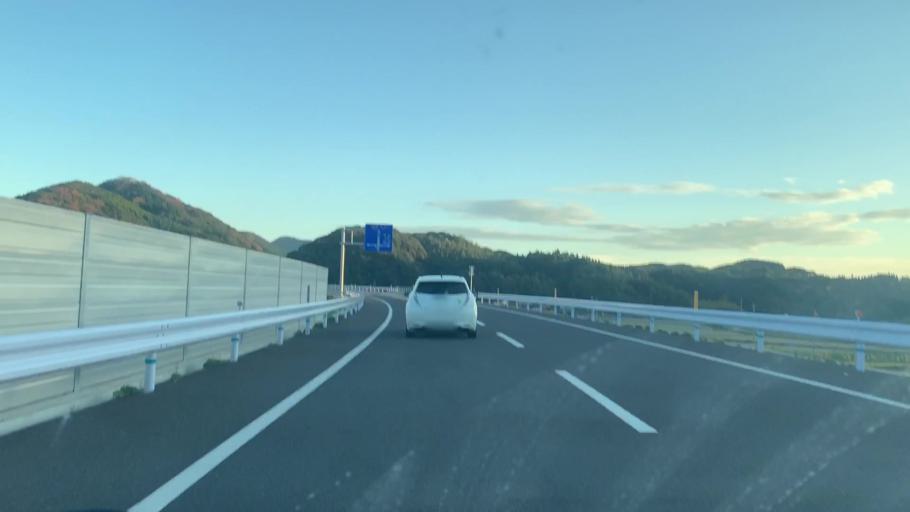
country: JP
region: Saga Prefecture
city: Takeocho-takeo
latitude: 33.2604
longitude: 129.9726
